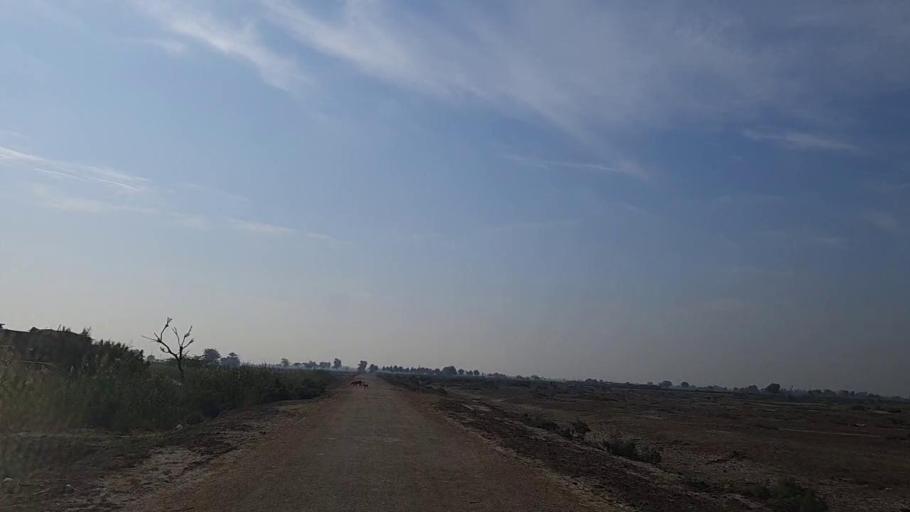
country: PK
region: Sindh
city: Mirpur Khas
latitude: 25.4995
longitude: 69.0001
